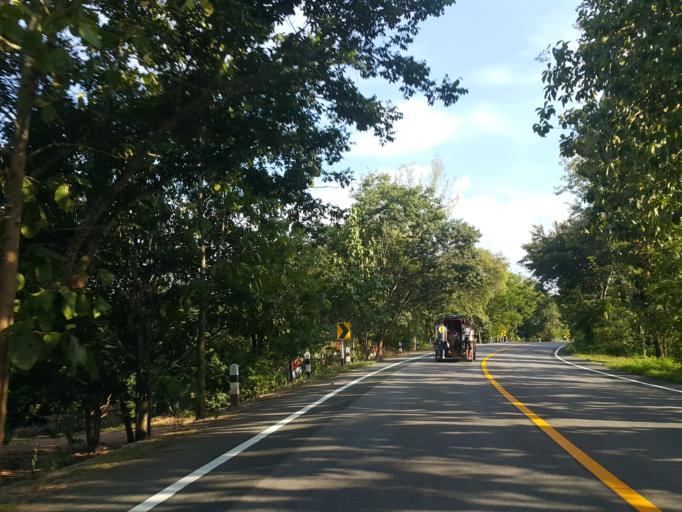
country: TH
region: Chiang Mai
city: Mae Taeng
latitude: 19.0979
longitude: 99.0009
